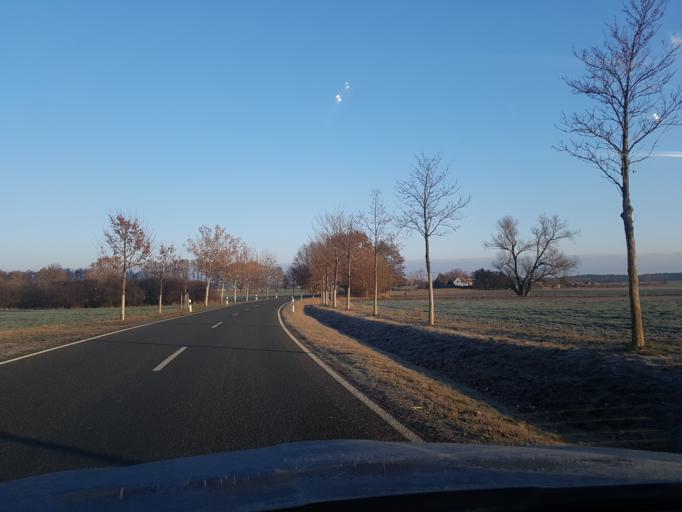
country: DE
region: Brandenburg
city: Herzberg
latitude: 51.6700
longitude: 13.2961
